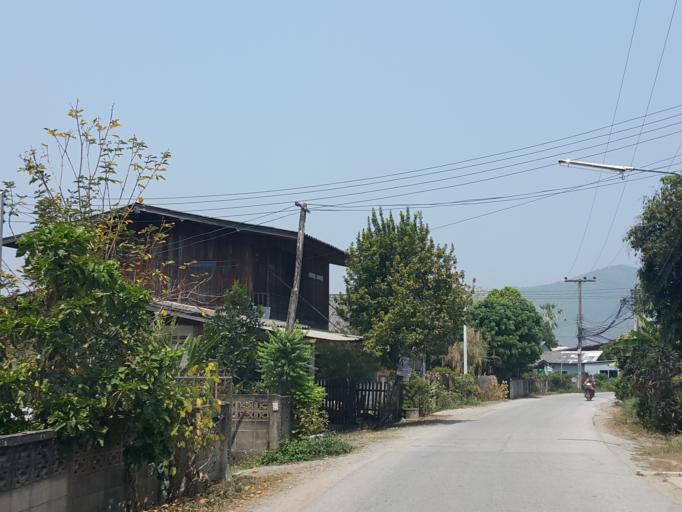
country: TH
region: Chiang Mai
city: Mae On
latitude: 18.7277
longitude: 99.2078
